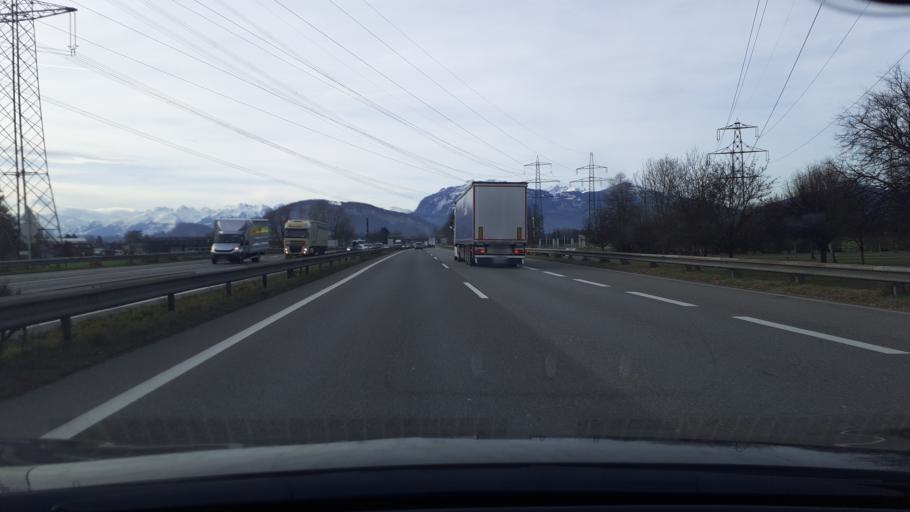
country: AT
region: Vorarlberg
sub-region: Politischer Bezirk Feldkirch
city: Altach
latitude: 47.3655
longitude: 9.6565
